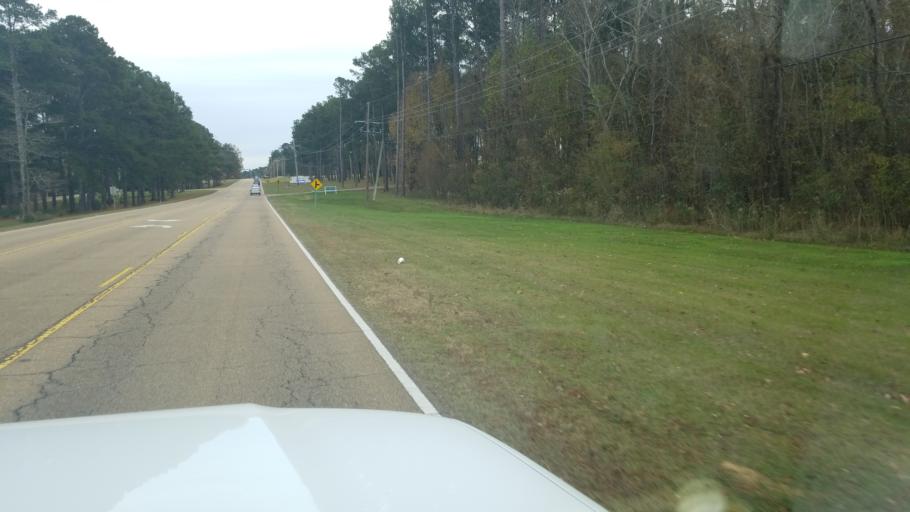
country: US
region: Mississippi
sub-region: Rankin County
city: Brandon
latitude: 32.3772
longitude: -90.0282
